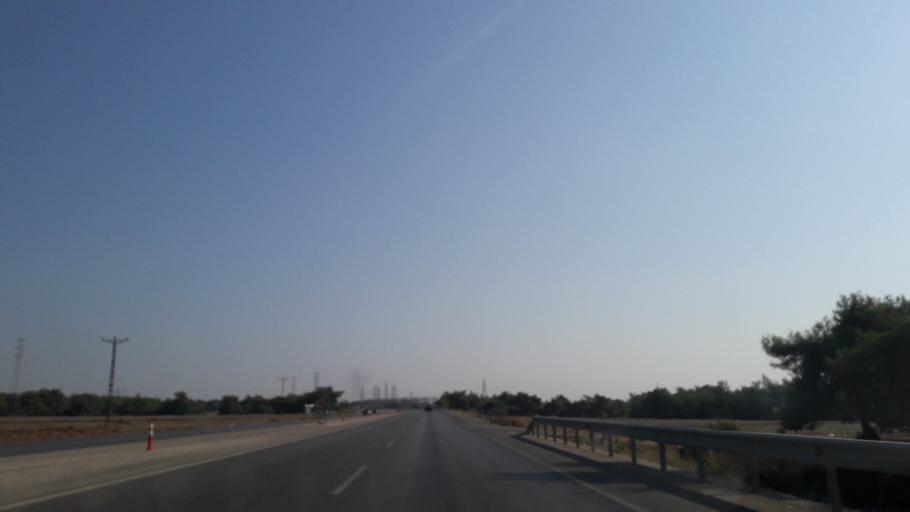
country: TR
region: Adana
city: Yakapinar
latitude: 37.0945
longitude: 35.4997
